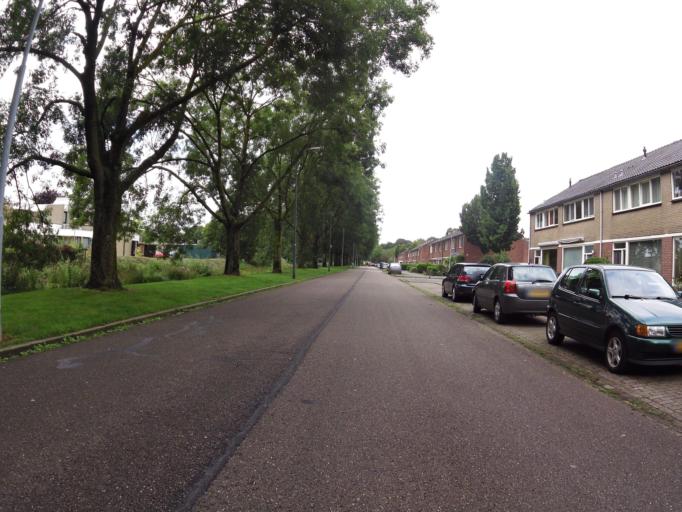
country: NL
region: North Brabant
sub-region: Gemeente 's-Hertogenbosch
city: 's-Hertogenbosch
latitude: 51.6977
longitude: 5.2585
